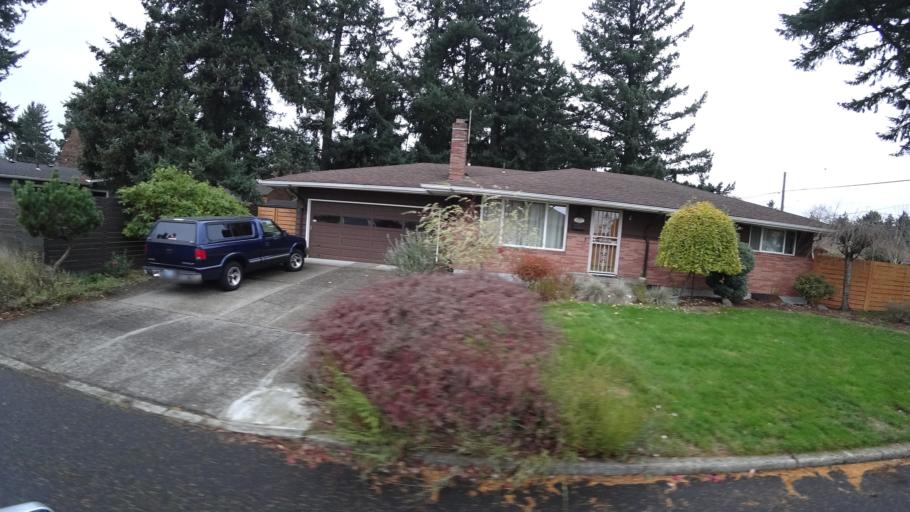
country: US
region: Oregon
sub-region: Multnomah County
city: Lents
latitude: 45.5299
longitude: -122.5532
